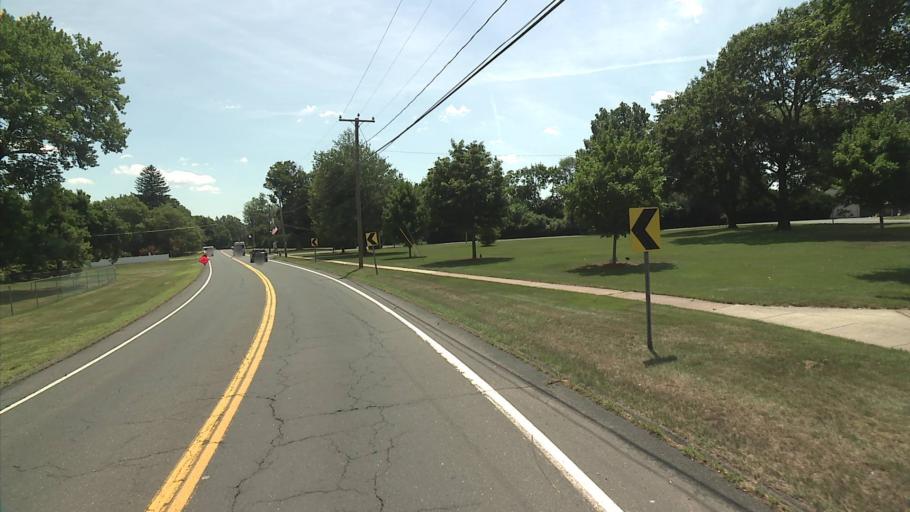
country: US
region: Connecticut
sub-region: Middlesex County
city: Cromwell
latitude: 41.5999
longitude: -72.6549
